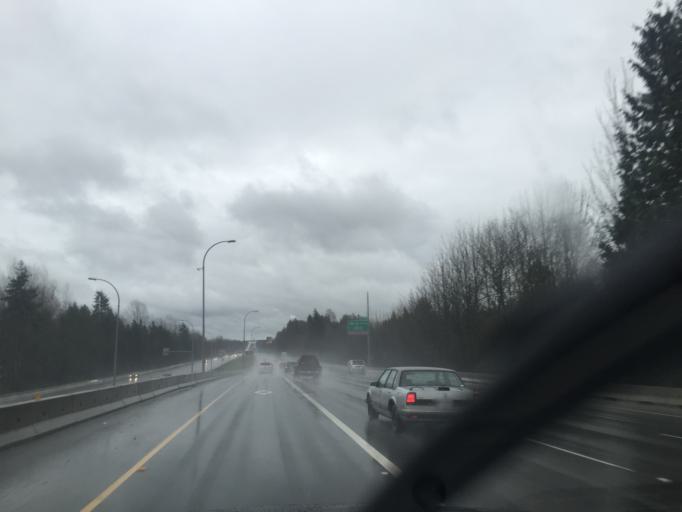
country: CA
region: British Columbia
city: Pitt Meadows
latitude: 49.1746
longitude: -122.7086
